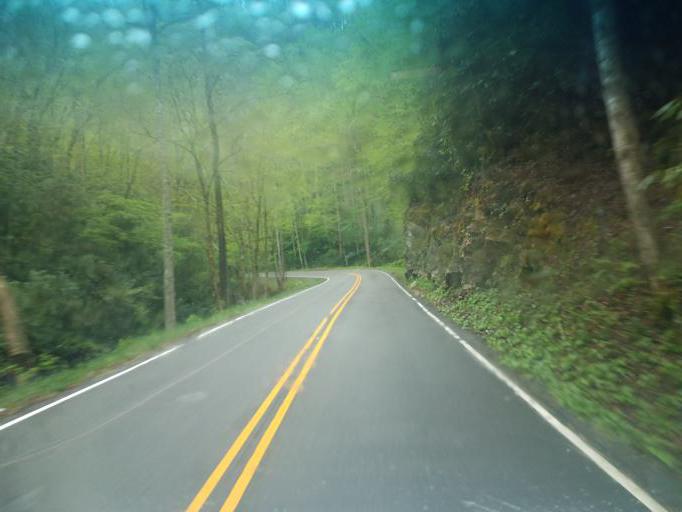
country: US
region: Virginia
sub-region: Washington County
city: Glade Spring
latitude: 36.6452
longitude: -81.7332
